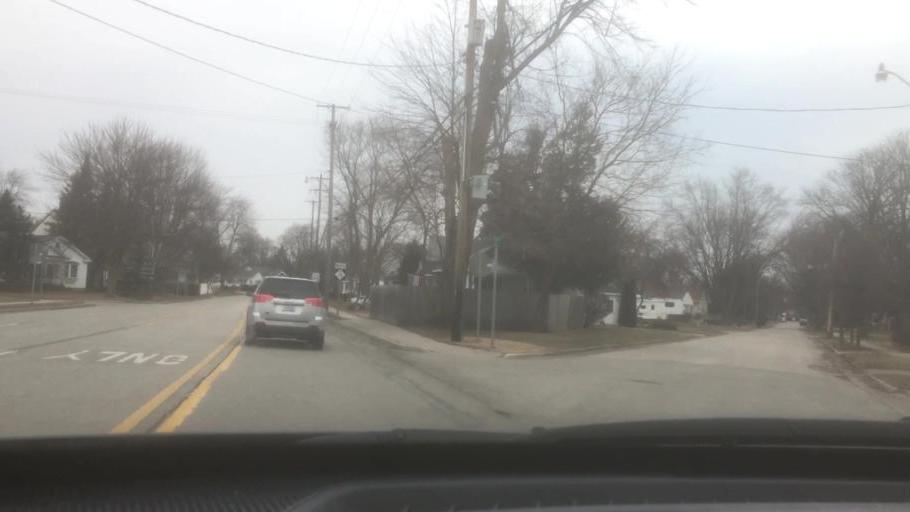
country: US
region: Michigan
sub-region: Bay County
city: Bay City
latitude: 43.5899
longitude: -83.8654
